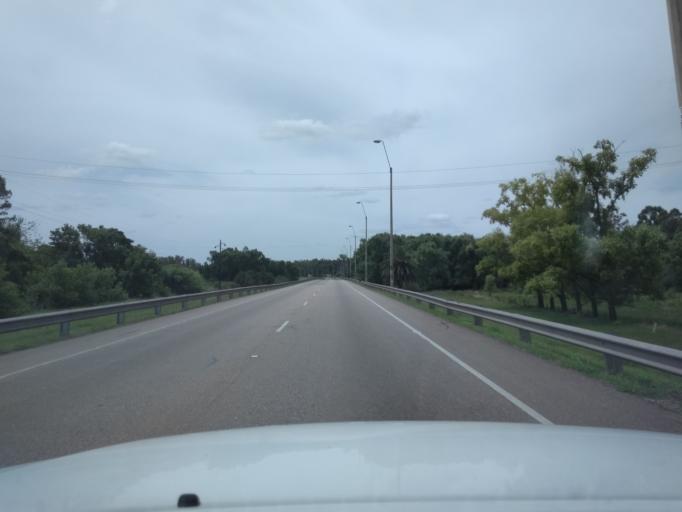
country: UY
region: Canelones
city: Canelones
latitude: -34.5347
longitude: -56.2723
